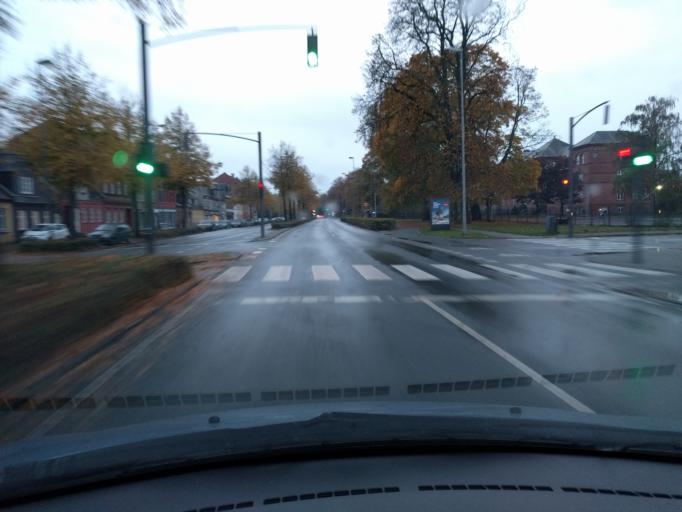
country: DK
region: South Denmark
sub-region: Odense Kommune
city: Odense
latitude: 55.3875
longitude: 10.3751
